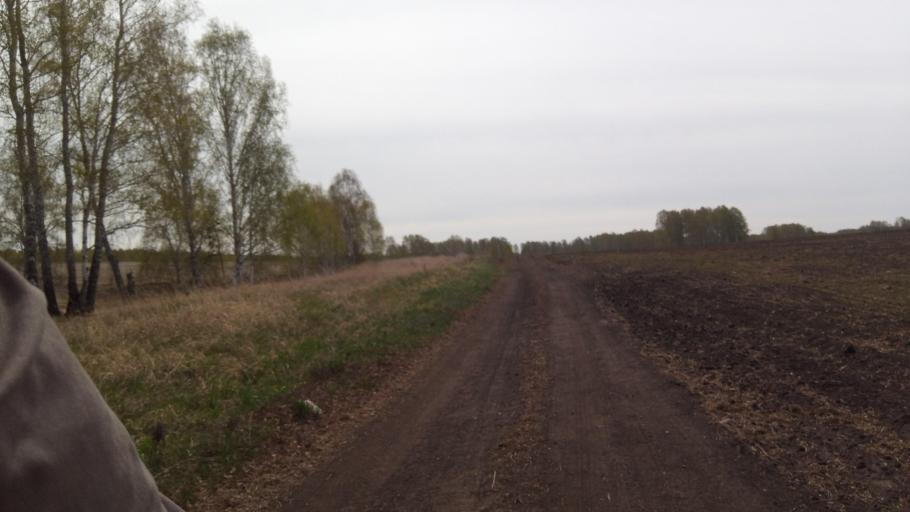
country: RU
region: Chelyabinsk
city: Timiryazevskiy
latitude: 55.0159
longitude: 60.8575
